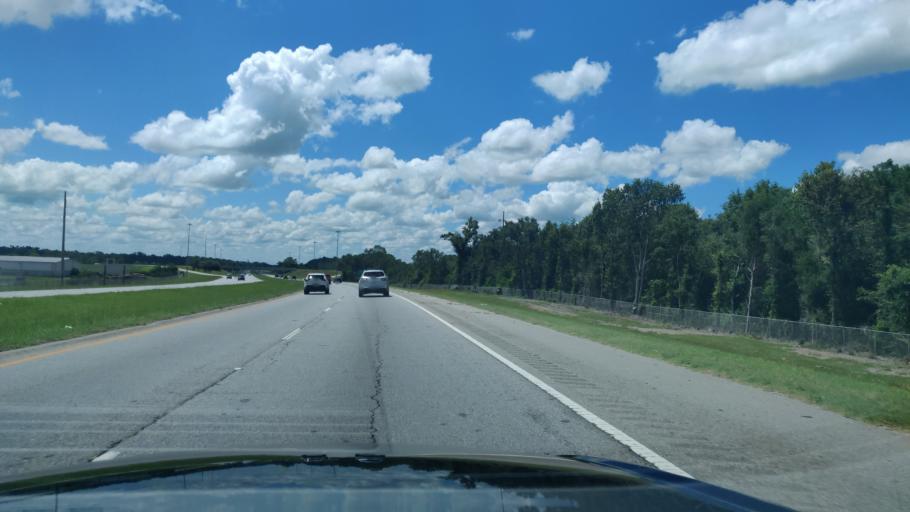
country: US
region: Georgia
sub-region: Dougherty County
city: Albany
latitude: 31.5900
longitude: -84.1183
